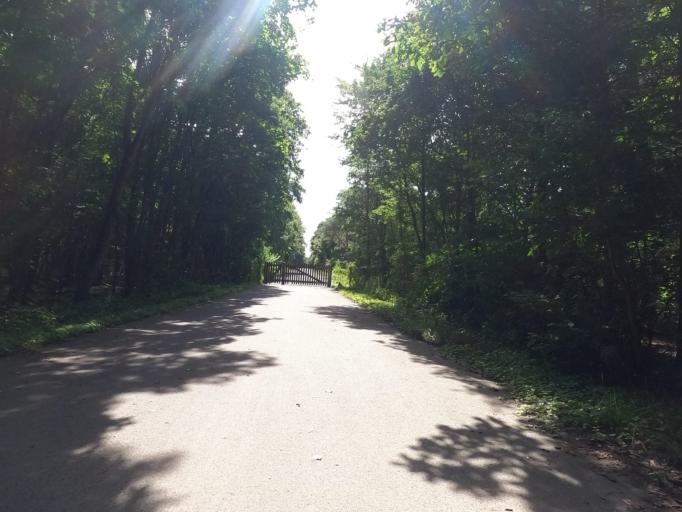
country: DE
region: Hesse
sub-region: Regierungsbezirk Darmstadt
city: Neu Isenburg
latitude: 50.0770
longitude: 8.7194
